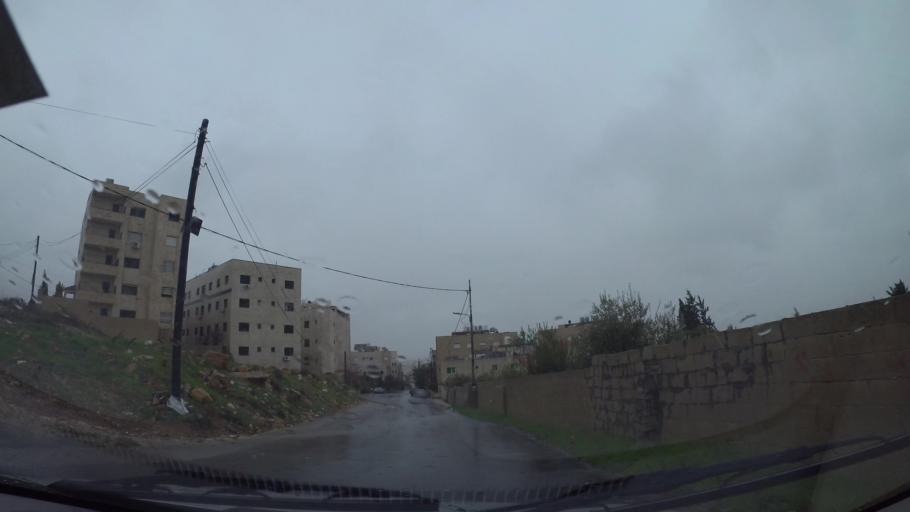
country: JO
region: Amman
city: Al Jubayhah
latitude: 32.0325
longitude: 35.8858
